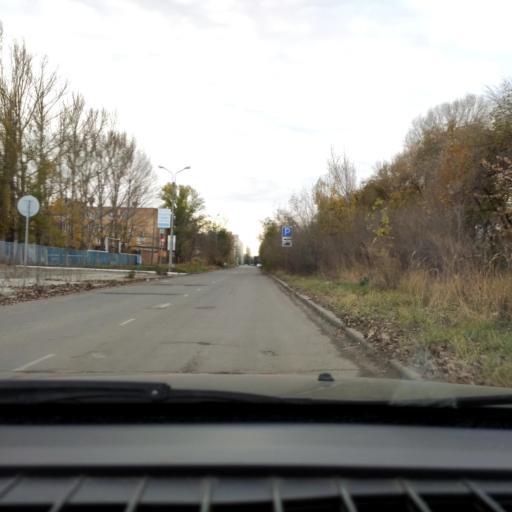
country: RU
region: Samara
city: Tol'yatti
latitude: 53.5537
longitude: 49.3136
